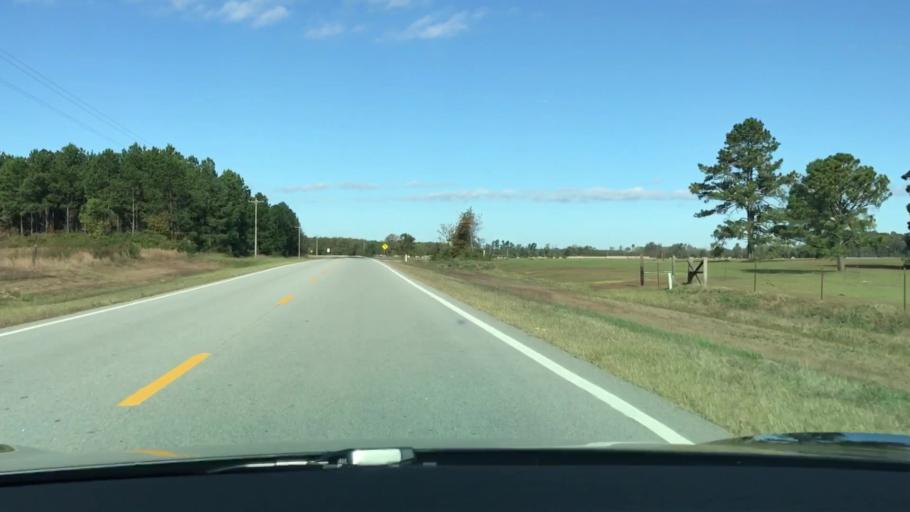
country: US
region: Georgia
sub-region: Glascock County
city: Gibson
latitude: 33.2920
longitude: -82.5106
